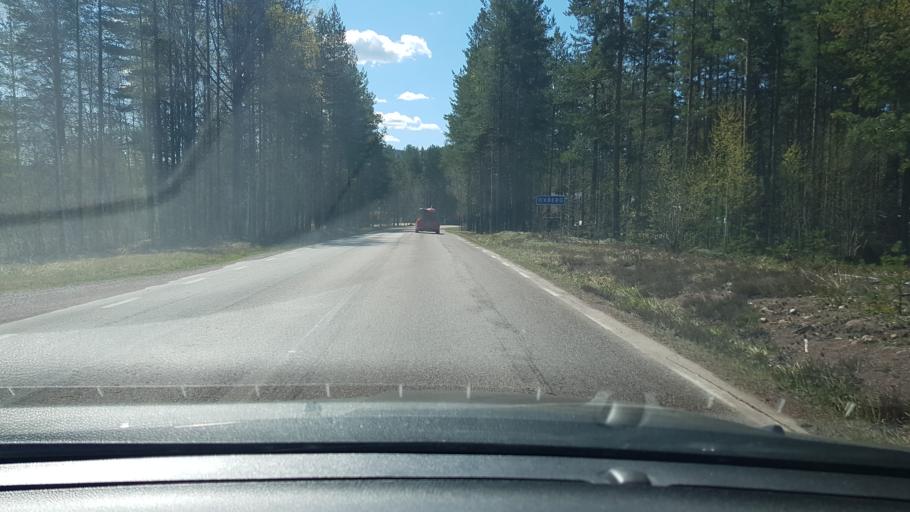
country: SE
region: Dalarna
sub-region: Alvdalens Kommun
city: AElvdalen
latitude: 61.1250
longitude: 14.1733
